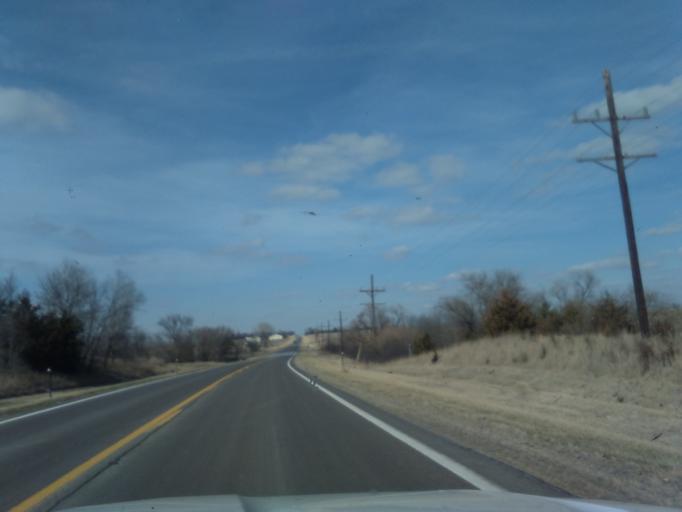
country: US
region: Nebraska
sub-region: Gage County
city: Beatrice
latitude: 40.1200
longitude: -96.9354
